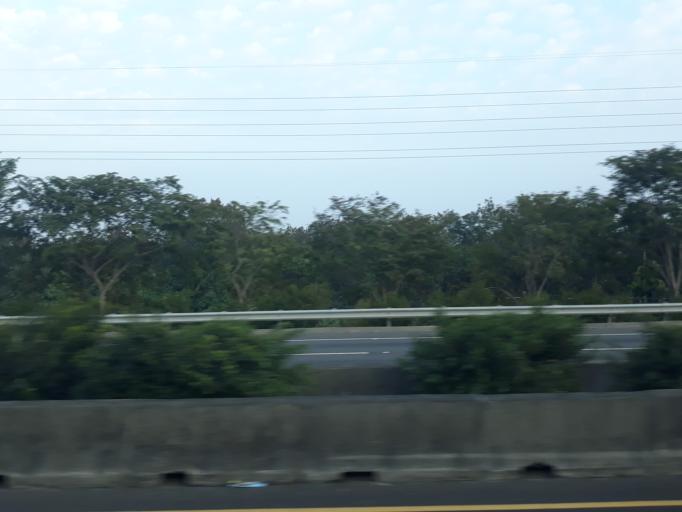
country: TW
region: Taiwan
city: Xinying
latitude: 23.2937
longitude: 120.2818
